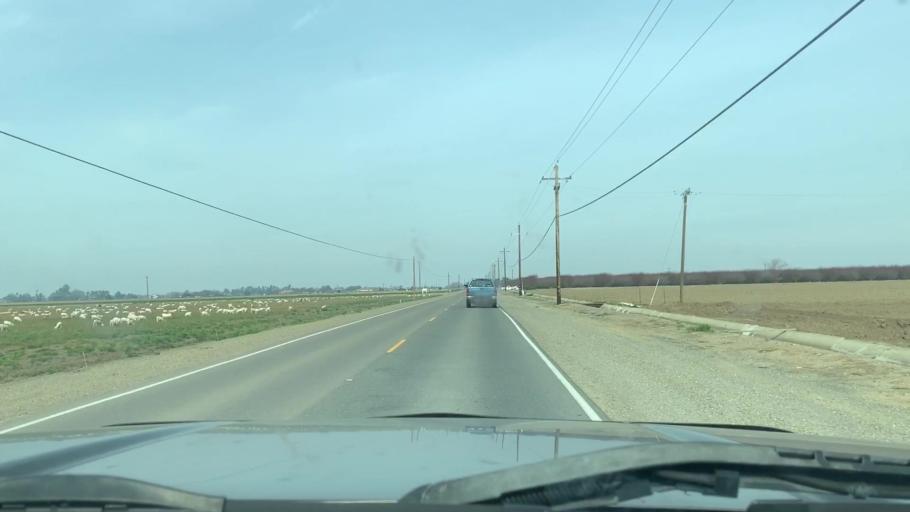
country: US
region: California
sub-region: Merced County
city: Los Banos
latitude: 37.0179
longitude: -120.8366
